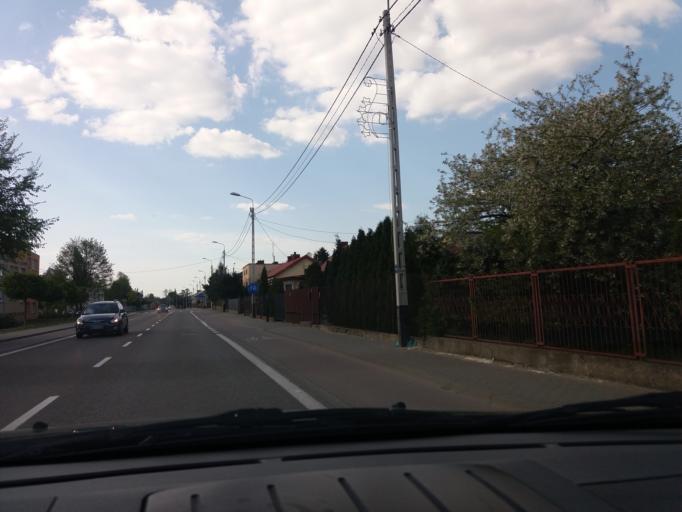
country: PL
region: Masovian Voivodeship
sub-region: Powiat mlawski
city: Mlawa
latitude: 53.1263
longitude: 20.3580
